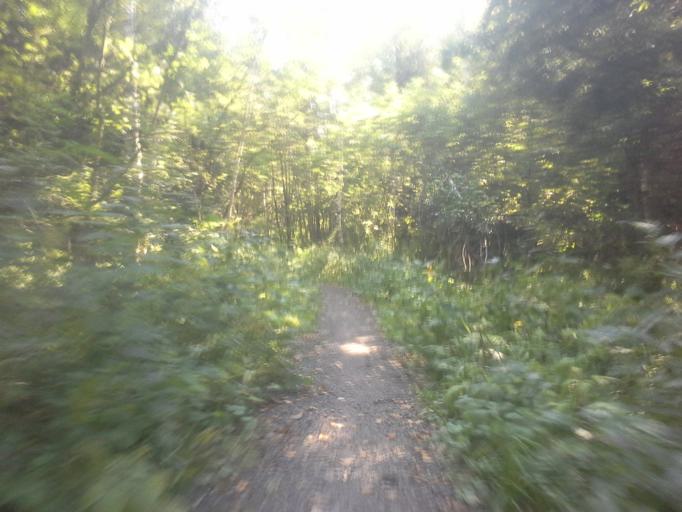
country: RU
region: Moskovskaya
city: Kievskij
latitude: 55.3415
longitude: 36.9676
